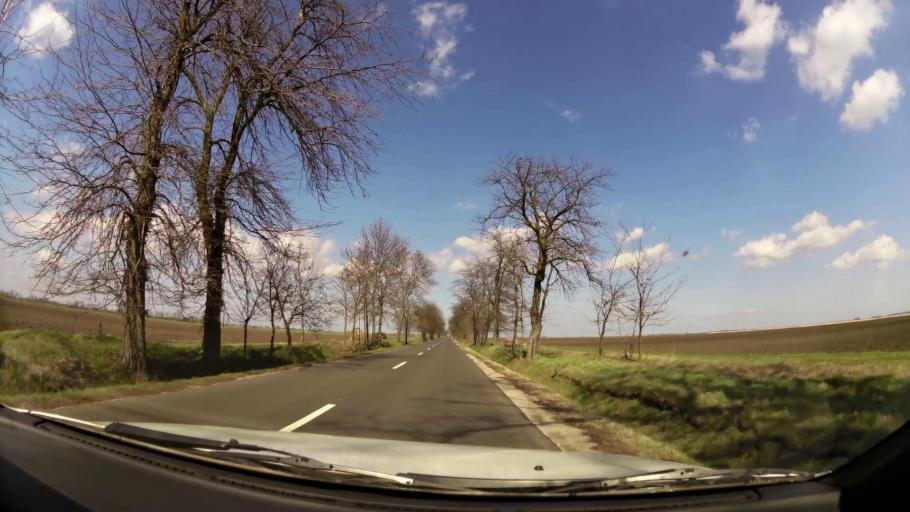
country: HU
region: Pest
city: Ujszilvas
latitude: 47.2833
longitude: 19.9281
